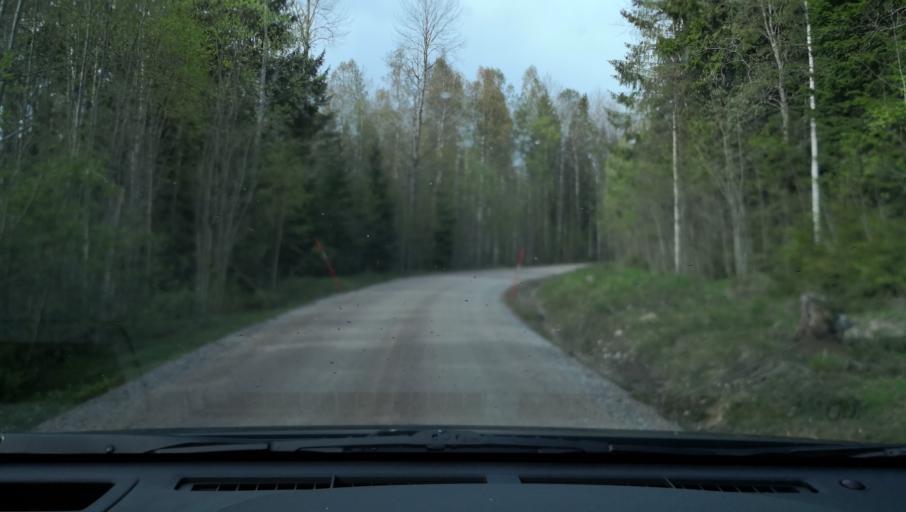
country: SE
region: Vaestmanland
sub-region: Fagersta Kommun
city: Fagersta
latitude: 60.1536
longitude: 15.6795
